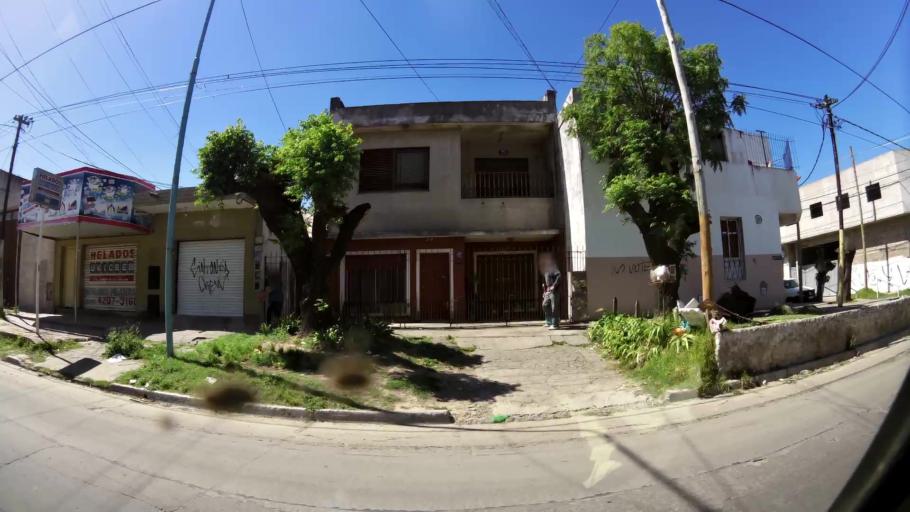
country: AR
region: Buenos Aires
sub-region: Partido de Quilmes
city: Quilmes
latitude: -34.7185
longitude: -58.3074
